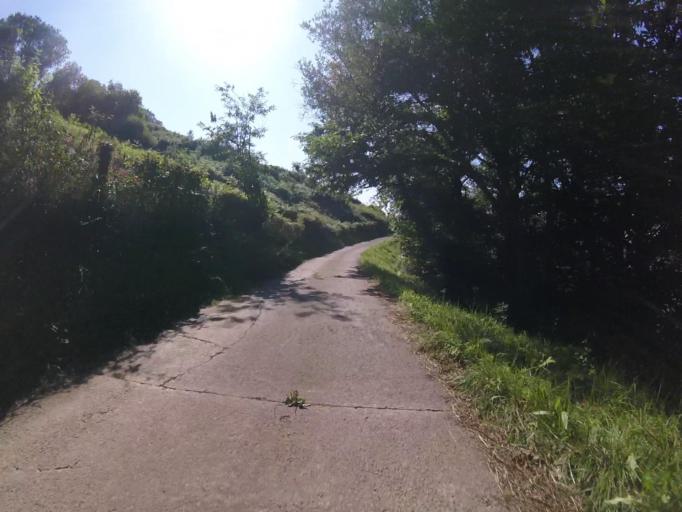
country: ES
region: Basque Country
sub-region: Provincia de Guipuzcoa
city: Astigarraga
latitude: 43.2775
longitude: -1.9319
